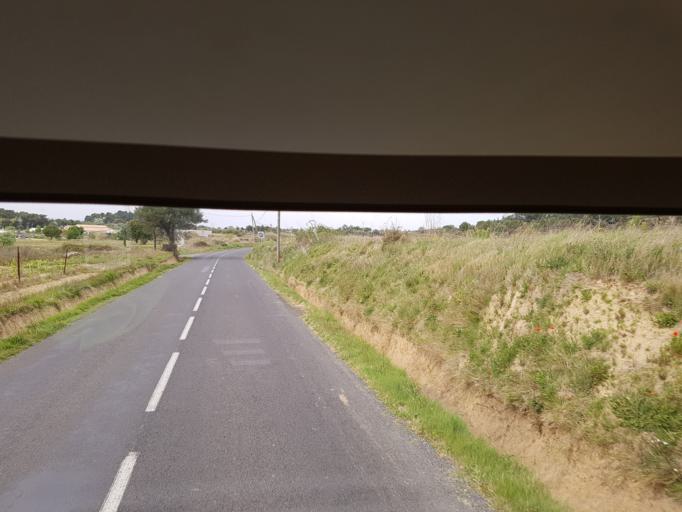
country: FR
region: Languedoc-Roussillon
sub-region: Departement de l'Aude
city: Fleury
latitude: 43.2169
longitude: 3.1333
